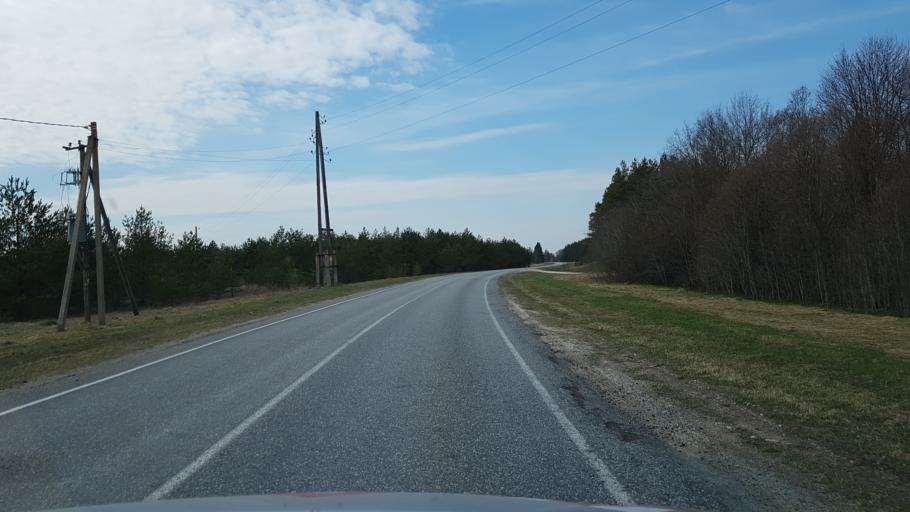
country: EE
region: Laeaene-Virumaa
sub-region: Haljala vald
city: Haljala
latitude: 59.4648
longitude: 26.1849
